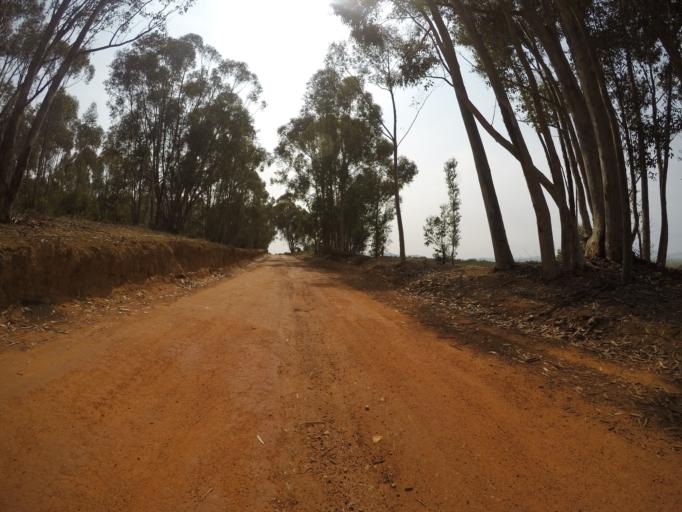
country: ZA
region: Western Cape
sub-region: West Coast District Municipality
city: Malmesbury
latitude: -33.4564
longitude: 18.7410
